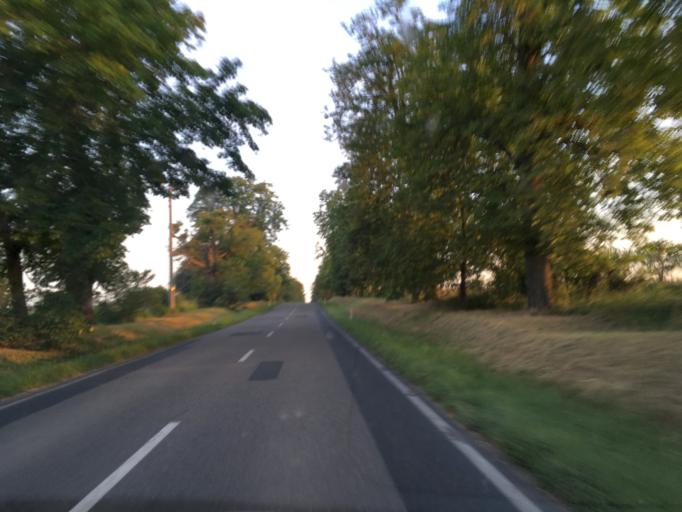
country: CZ
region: South Moravian
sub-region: Okres Breclav
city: Lednice
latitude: 48.7921
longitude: 16.7971
